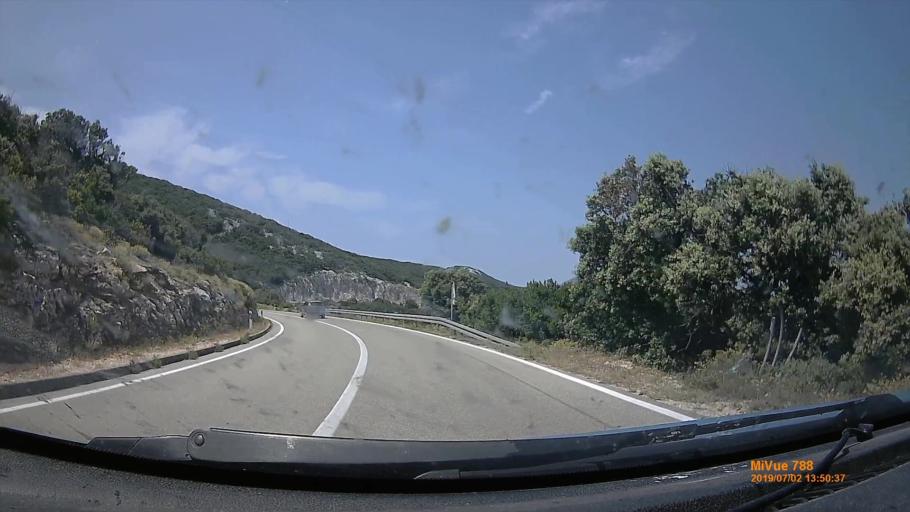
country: HR
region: Primorsko-Goranska
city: Mali Losinj
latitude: 44.5984
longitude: 14.4093
